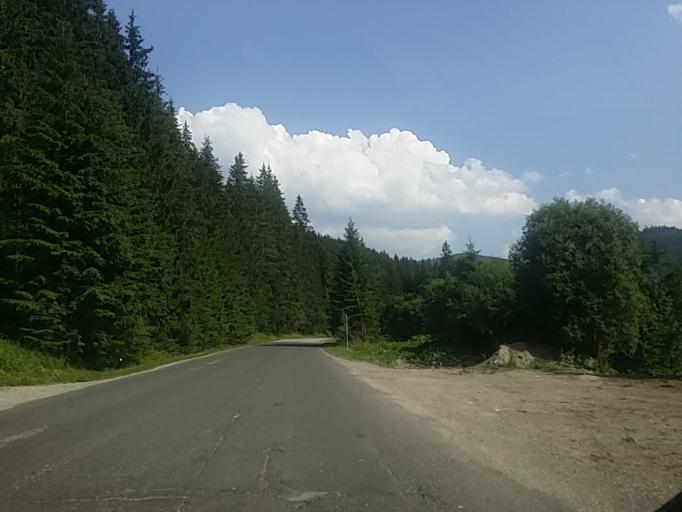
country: SK
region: Banskobystricky
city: Revuca
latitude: 48.8183
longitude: 20.1456
